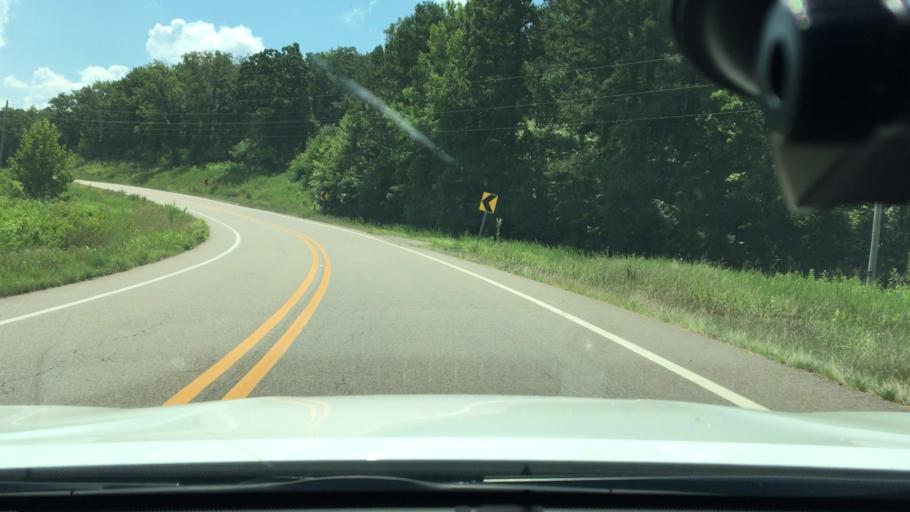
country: US
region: Arkansas
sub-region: Logan County
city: Paris
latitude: 35.2567
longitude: -93.6824
